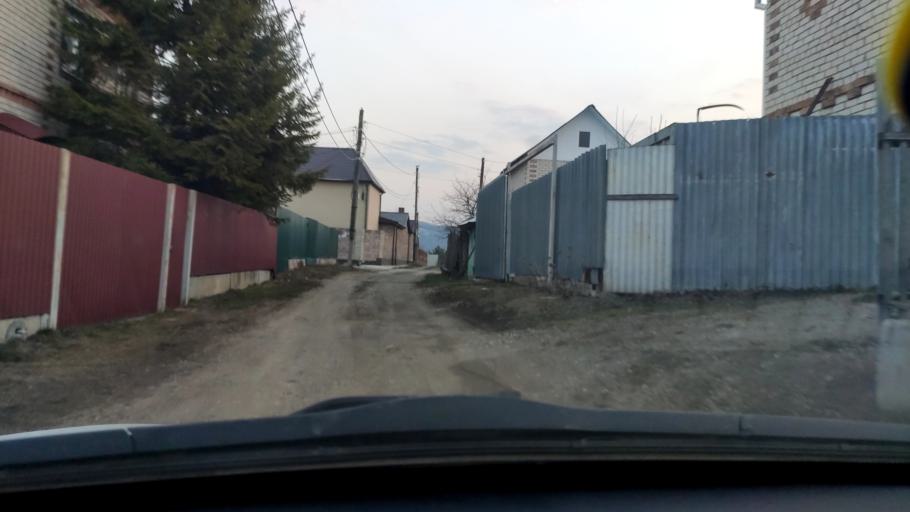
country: RU
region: Samara
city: Zhigulevsk
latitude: 53.4522
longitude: 49.5247
